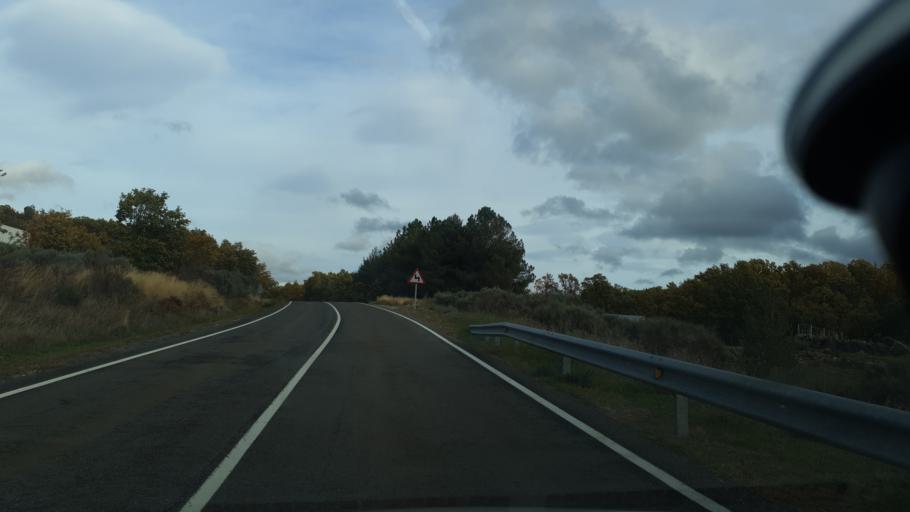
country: ES
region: Castille and Leon
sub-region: Provincia de Avila
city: Hoyocasero
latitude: 40.3900
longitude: -4.9993
